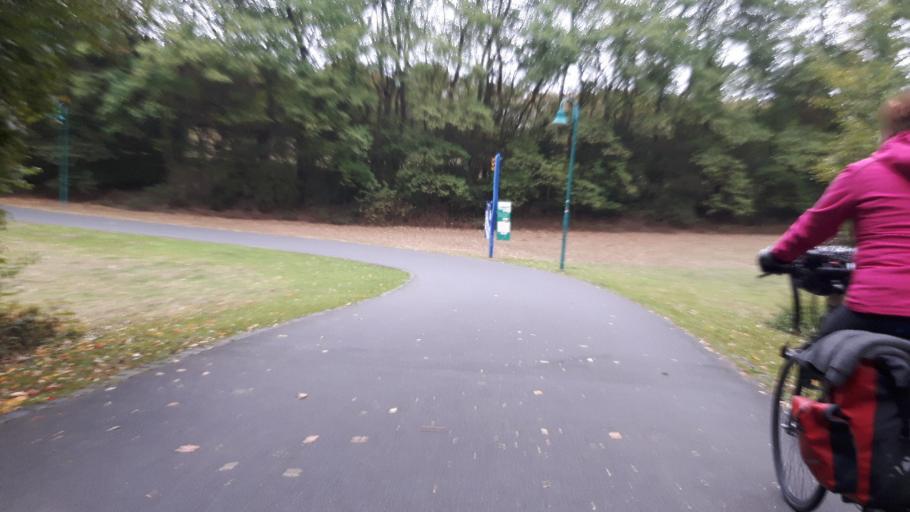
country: DE
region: North Rhine-Westphalia
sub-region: Regierungsbezirk Koln
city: Konigswinter
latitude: 50.7191
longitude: 7.1471
